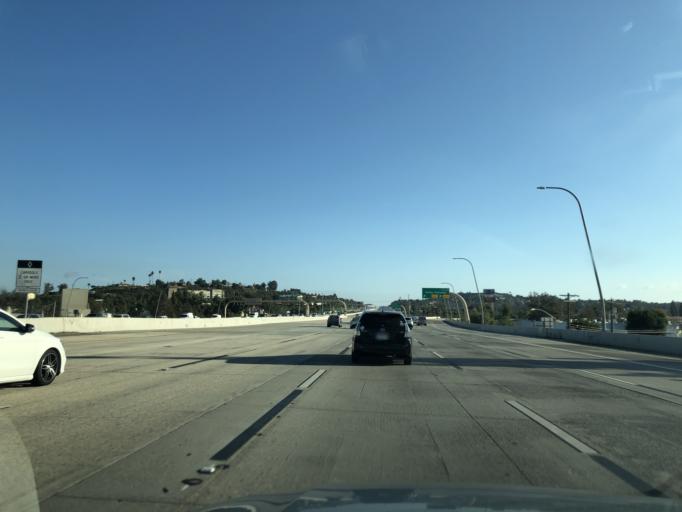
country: US
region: California
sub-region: San Diego County
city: Escondido
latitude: 33.1207
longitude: -117.1028
